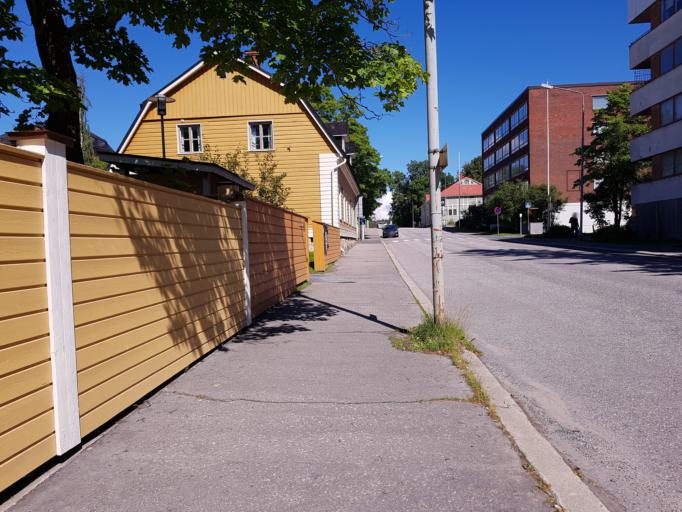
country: FI
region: Northern Savo
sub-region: Kuopio
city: Kuopio
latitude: 62.8895
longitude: 27.6858
